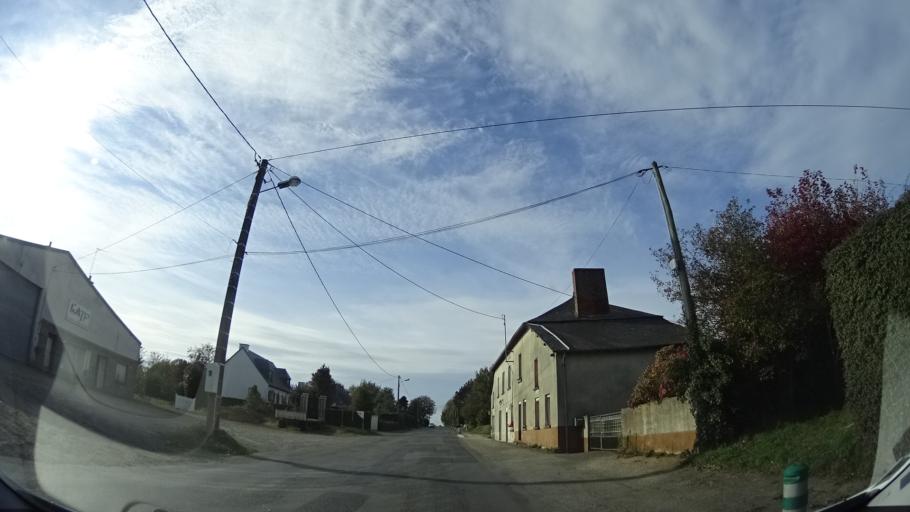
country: FR
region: Brittany
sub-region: Departement d'Ille-et-Vilaine
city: Romille
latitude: 48.2153
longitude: -1.8998
